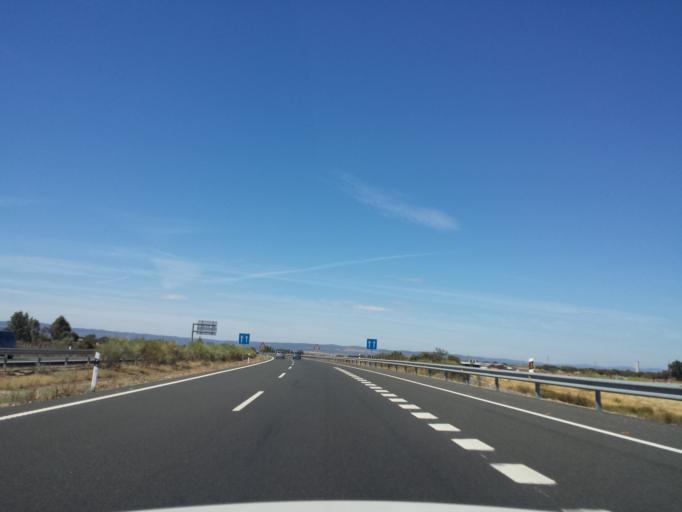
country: ES
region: Extremadura
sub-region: Provincia de Caceres
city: Millanes
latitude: 39.8637
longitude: -5.6056
